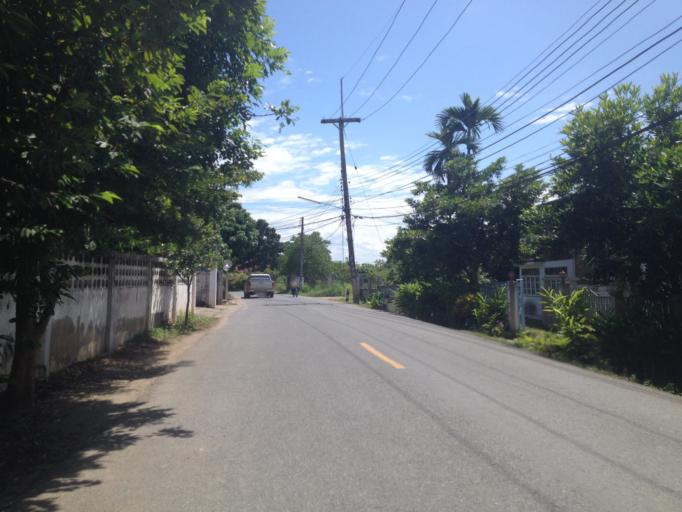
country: TH
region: Chiang Mai
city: Hang Dong
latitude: 18.6833
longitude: 98.9274
